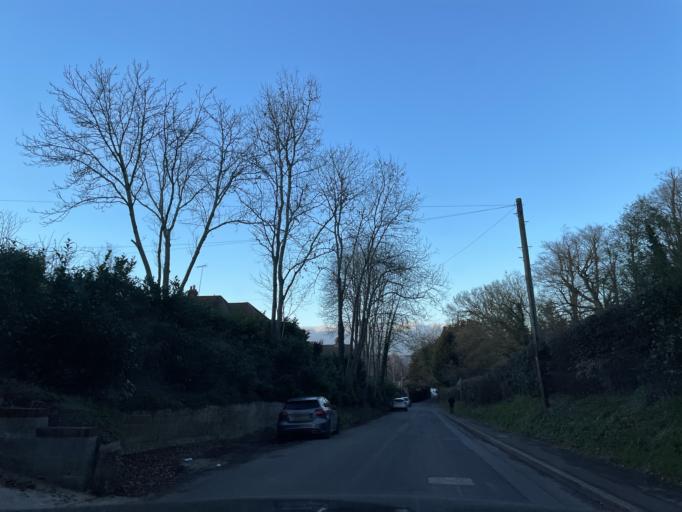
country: GB
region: England
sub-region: Kent
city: Halstead
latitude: 51.2749
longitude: 0.1273
